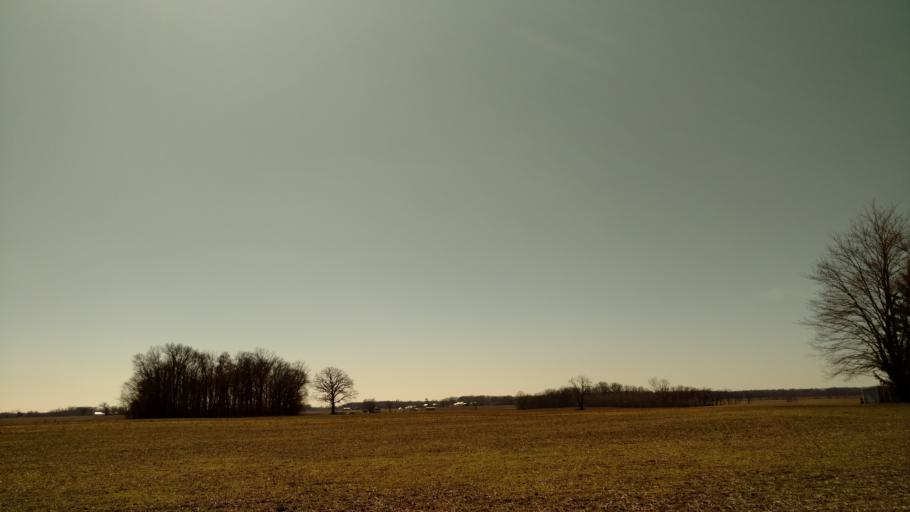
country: US
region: Ohio
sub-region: Marion County
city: Marion
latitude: 40.4938
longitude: -83.0787
